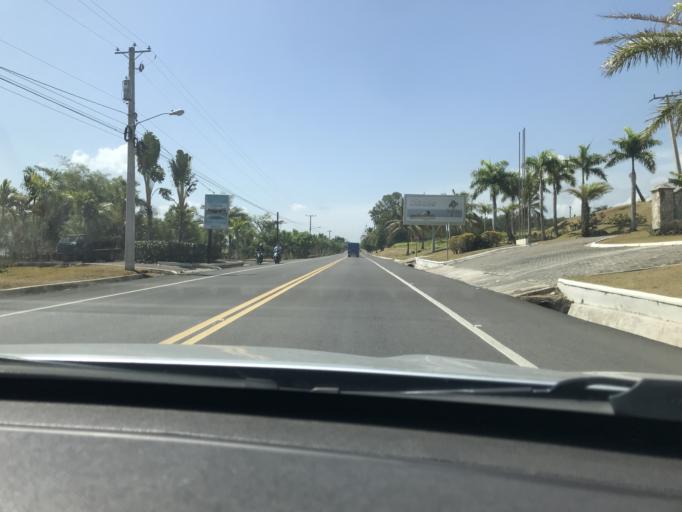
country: DO
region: Puerto Plata
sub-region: Puerto Plata
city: Puerto Plata
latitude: 19.7350
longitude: -70.6294
